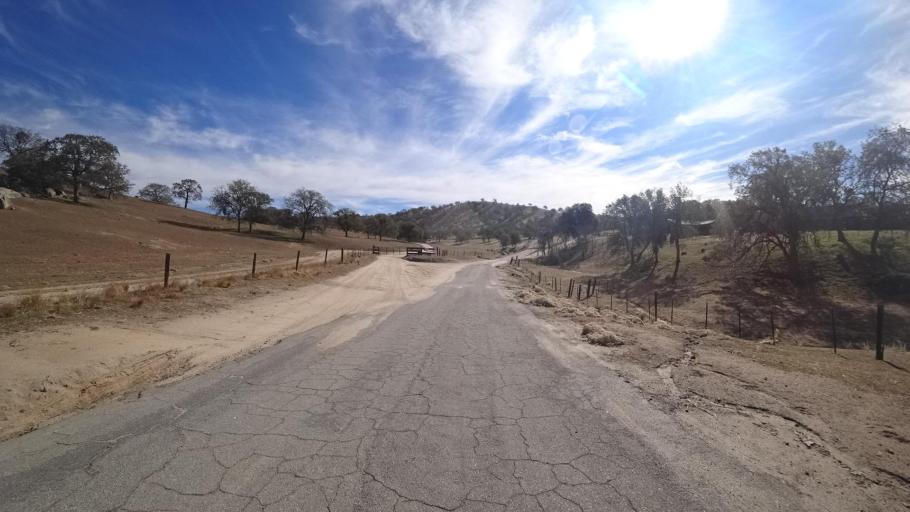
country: US
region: California
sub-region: Kern County
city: Oildale
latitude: 35.5811
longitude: -118.8142
